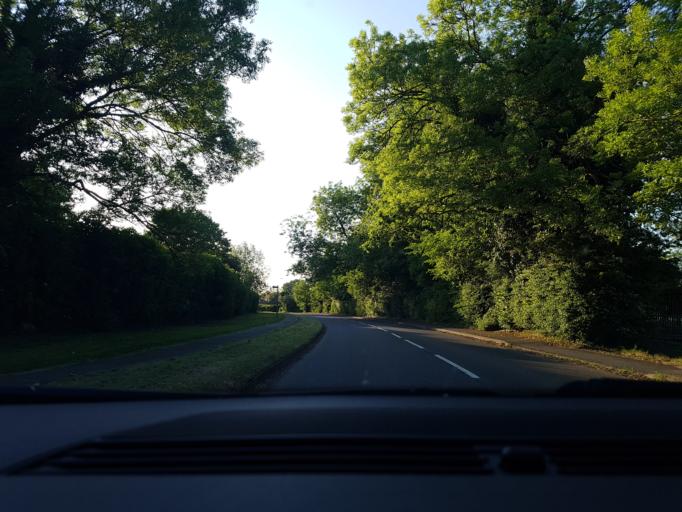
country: GB
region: England
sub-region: Buckinghamshire
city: Buckingham
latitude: 51.9956
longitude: -0.9760
